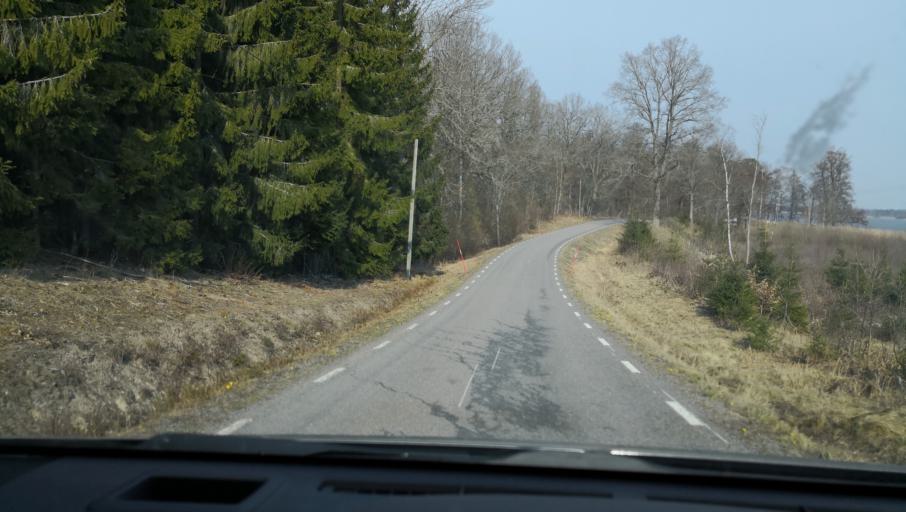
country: SE
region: OErebro
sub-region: Lindesbergs Kommun
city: Frovi
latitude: 59.3978
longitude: 15.4094
